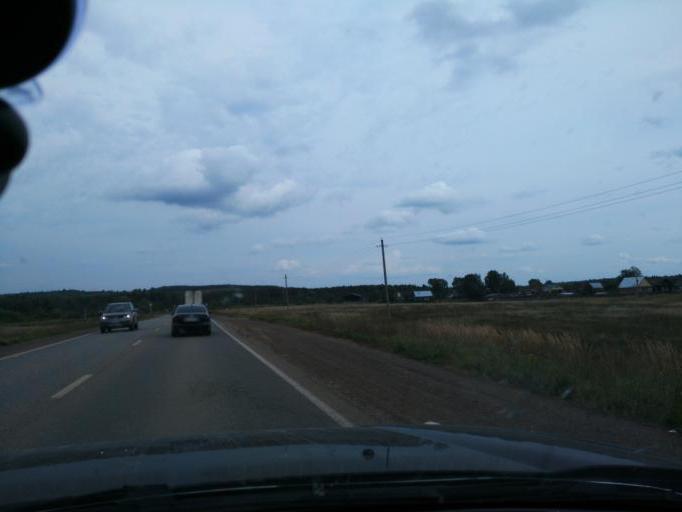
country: RU
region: Perm
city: Kuyeda
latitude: 56.4526
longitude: 55.6123
